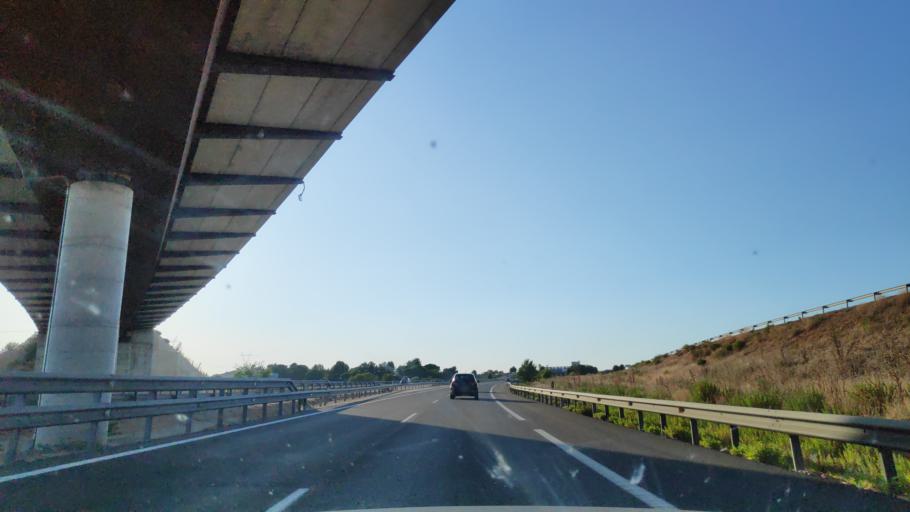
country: ES
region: Castille-La Mancha
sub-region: Provincia de Cuenca
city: Tarancon
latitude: 39.9998
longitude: -3.0219
